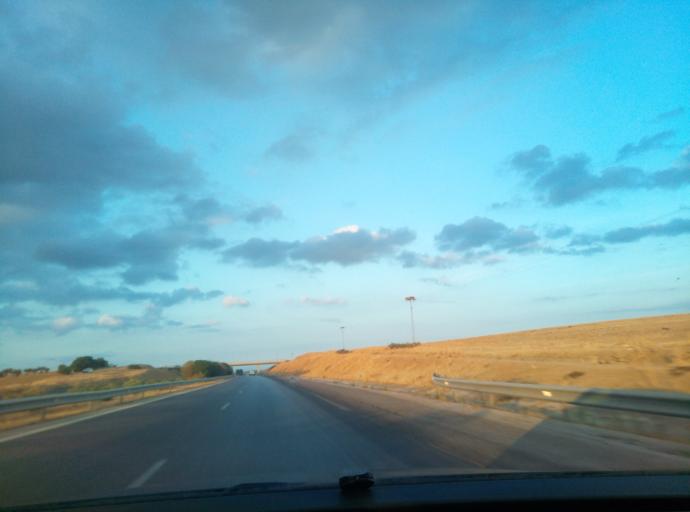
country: TN
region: Tunis
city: Oued Lill
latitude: 36.7073
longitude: 9.9649
